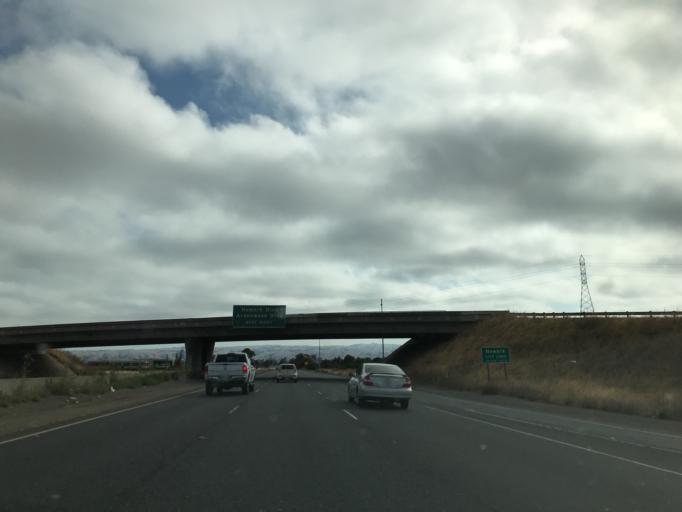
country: US
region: California
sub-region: Alameda County
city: Newark
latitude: 37.5397
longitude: -122.0681
